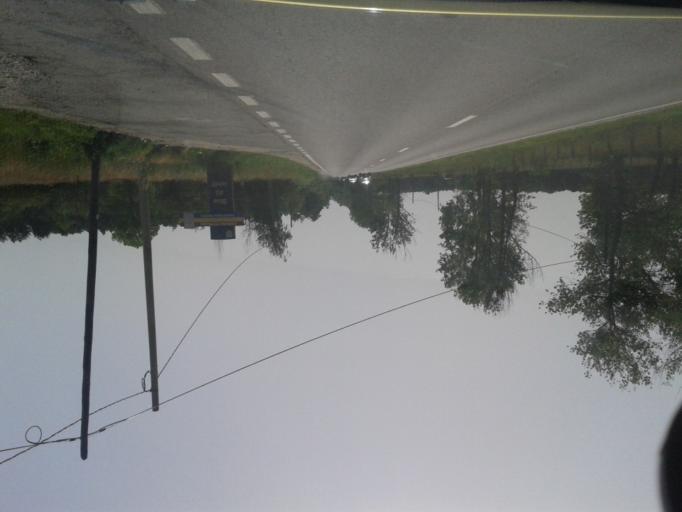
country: RO
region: Arges
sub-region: Comuna Moraresti
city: Moraresti
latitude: 45.0062
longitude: 24.5801
